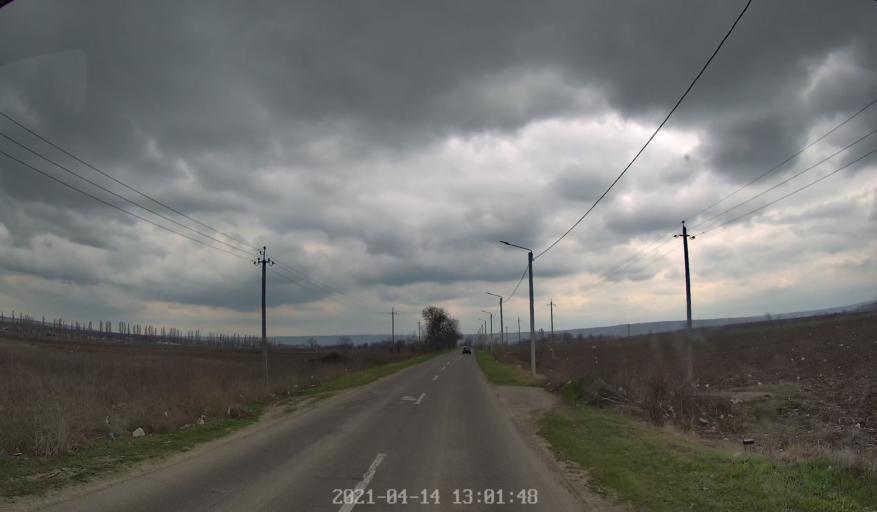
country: MD
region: Chisinau
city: Vadul lui Voda
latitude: 47.1287
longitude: 29.1141
